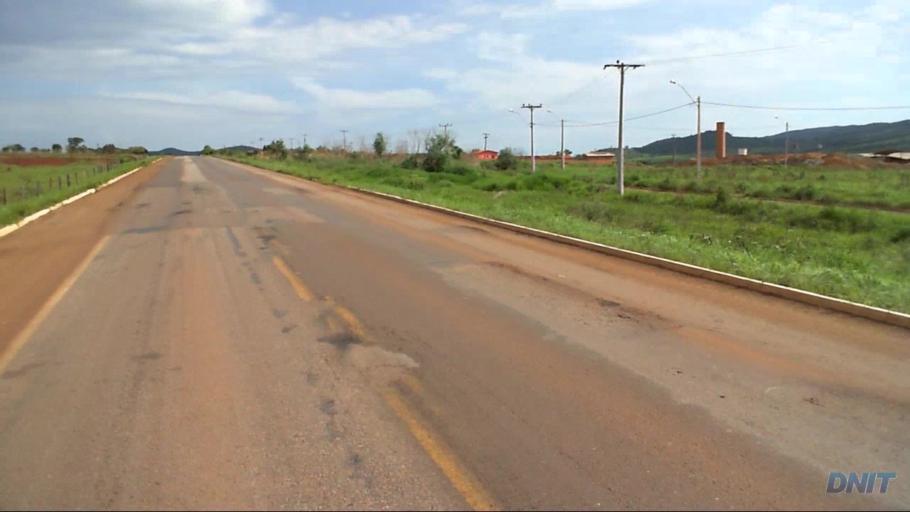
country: BR
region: Goias
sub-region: Barro Alto
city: Barro Alto
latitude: -14.9761
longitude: -48.9299
